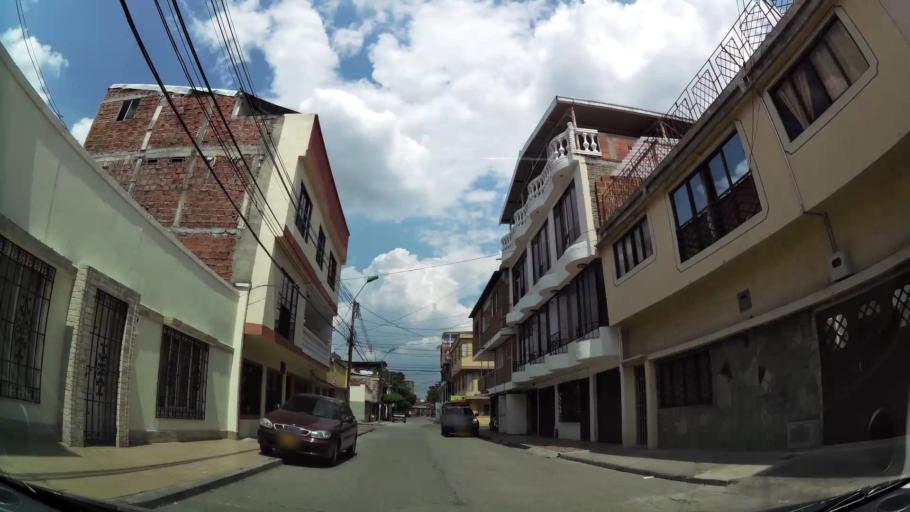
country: CO
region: Valle del Cauca
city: Cali
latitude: 3.4627
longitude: -76.5038
